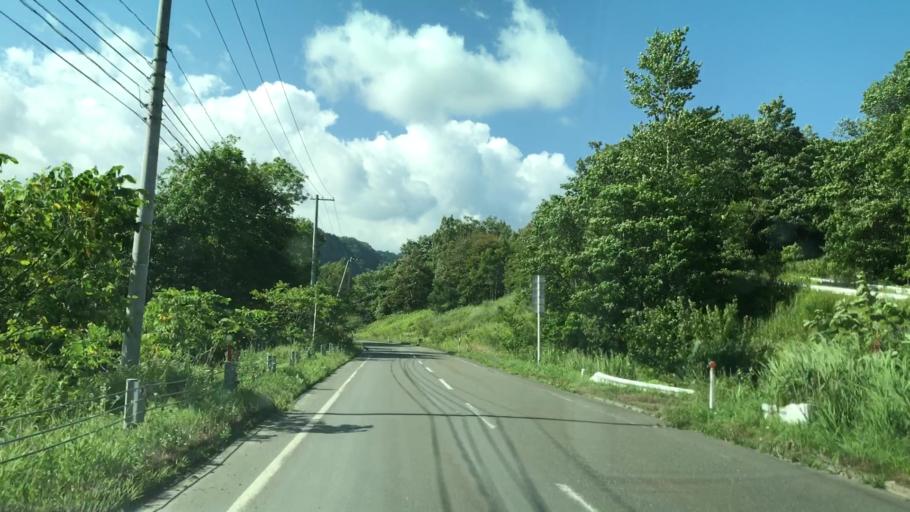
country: JP
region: Hokkaido
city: Shimo-furano
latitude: 42.8490
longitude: 142.4216
